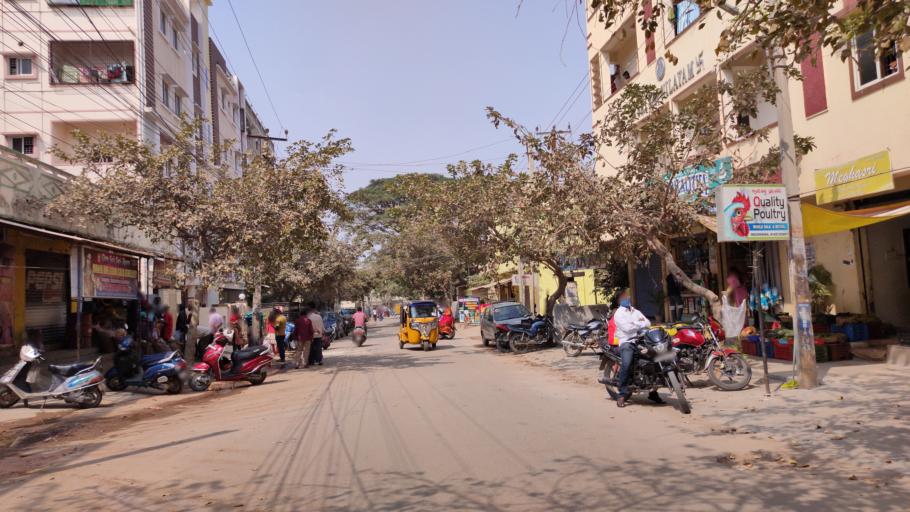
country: IN
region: Telangana
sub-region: Rangareddi
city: Quthbullapur
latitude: 17.4924
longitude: 78.4607
